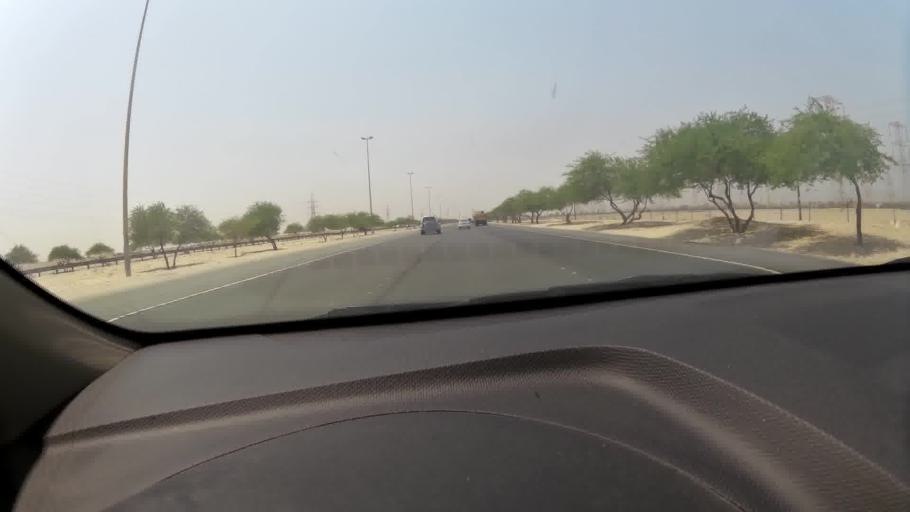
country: KW
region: Al Ahmadi
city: Al Fahahil
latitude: 28.9367
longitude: 48.1587
